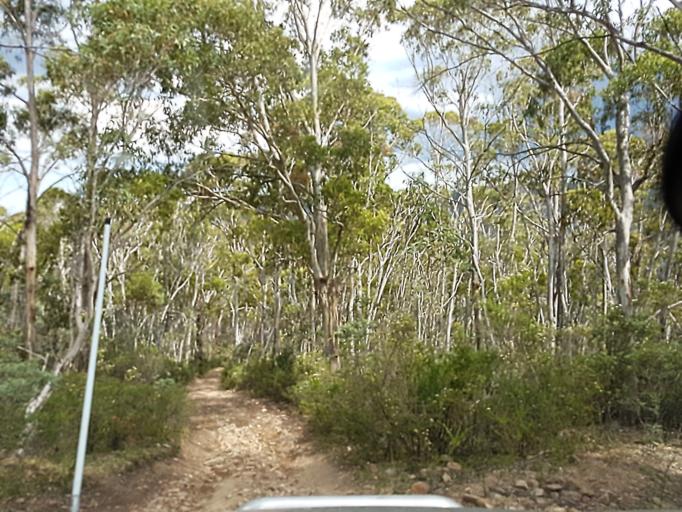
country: AU
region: New South Wales
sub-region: Snowy River
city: Jindabyne
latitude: -36.8801
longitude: 148.2029
